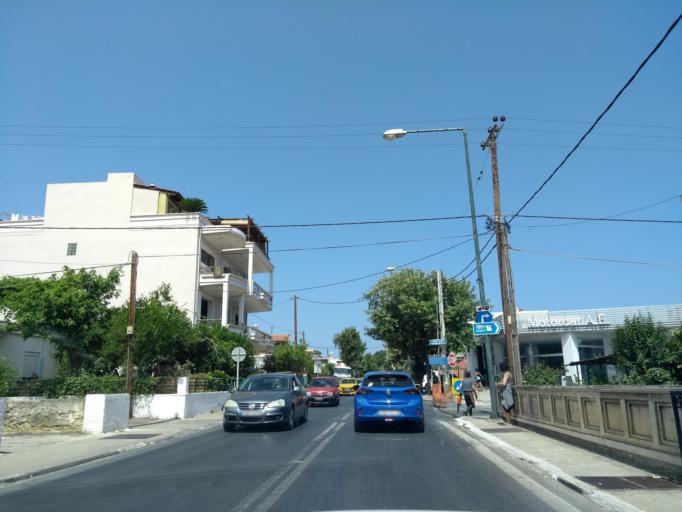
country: GR
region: Crete
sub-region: Nomos Chanias
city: Tsikalaria
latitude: 35.4880
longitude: 24.0605
